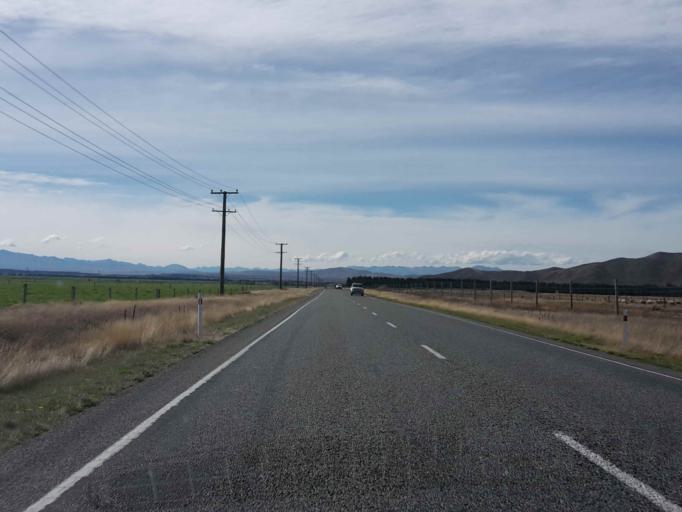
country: NZ
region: Otago
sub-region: Queenstown-Lakes District
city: Wanaka
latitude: -44.3313
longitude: 170.0322
